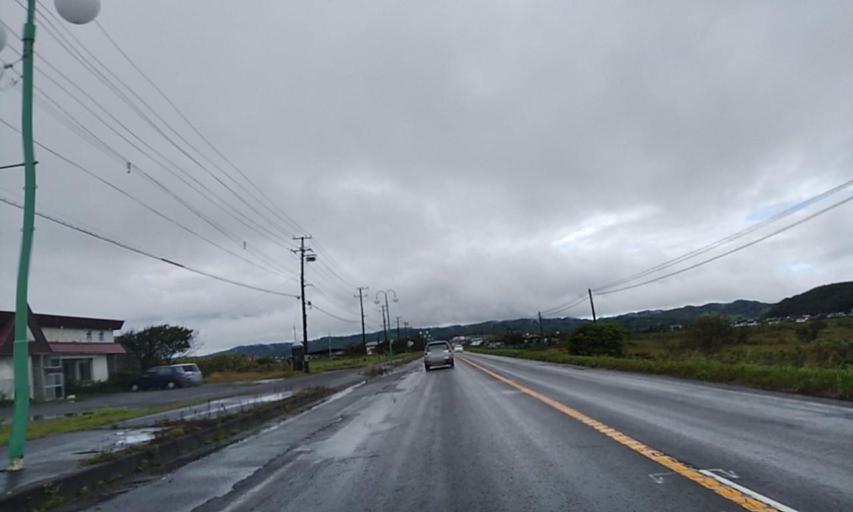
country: JP
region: Hokkaido
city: Kushiro
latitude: 42.9838
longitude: 144.1615
